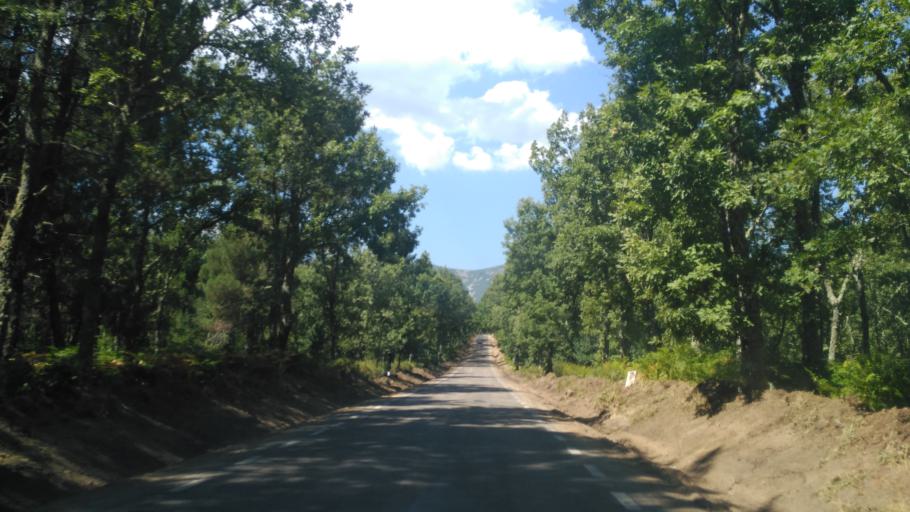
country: ES
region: Castille and Leon
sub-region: Provincia de Salamanca
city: Nava de Francia
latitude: 40.5243
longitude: -6.1244
